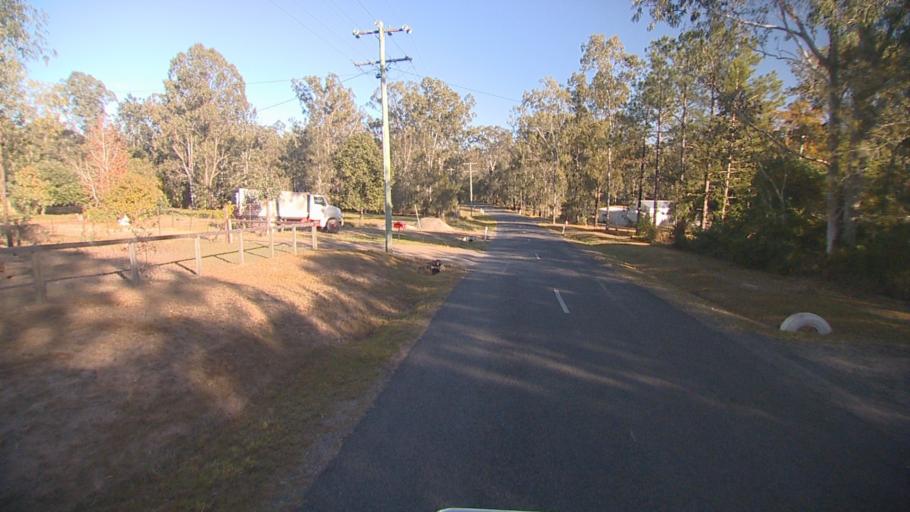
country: AU
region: Queensland
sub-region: Logan
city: North Maclean
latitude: -27.7836
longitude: 152.9759
